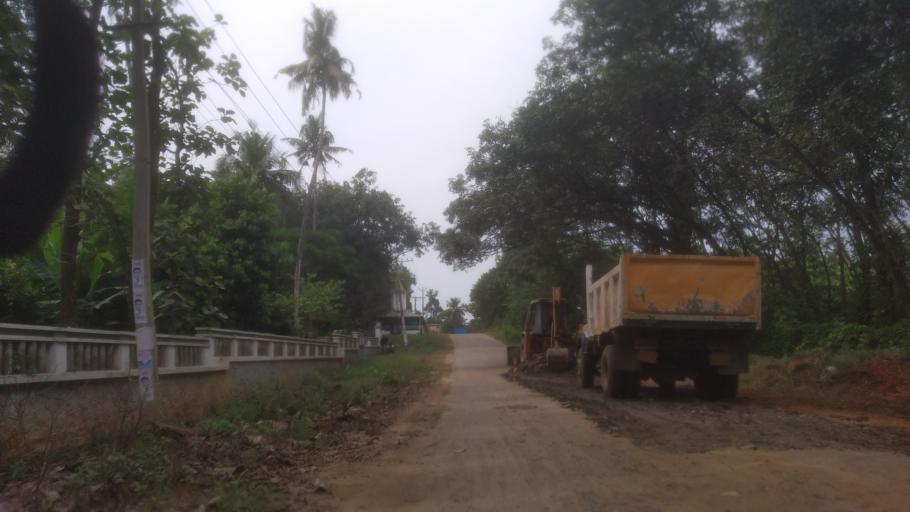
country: IN
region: Kerala
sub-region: Ernakulam
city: Perumbavoor
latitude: 10.0491
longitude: 76.5247
